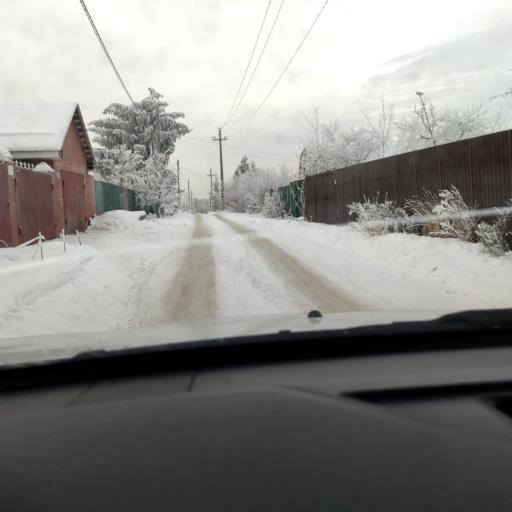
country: RU
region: Samara
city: Petra-Dubrava
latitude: 53.3008
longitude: 50.2514
